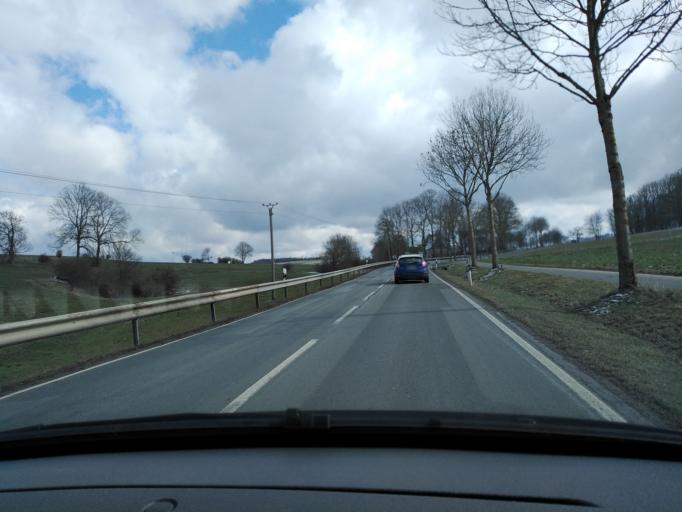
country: DE
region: North Rhine-Westphalia
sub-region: Regierungsbezirk Arnsberg
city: Brilon
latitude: 51.4050
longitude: 8.6219
